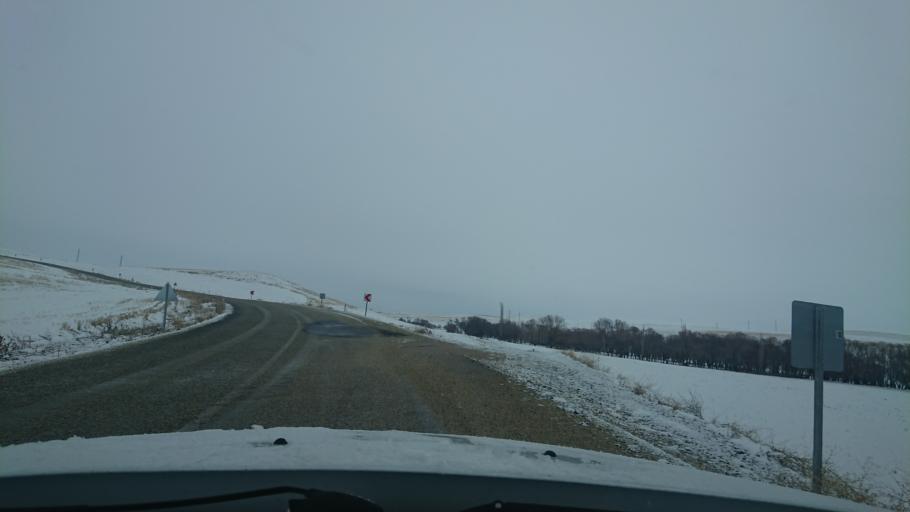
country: TR
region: Aksaray
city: Agacoren
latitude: 38.7611
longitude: 33.8704
